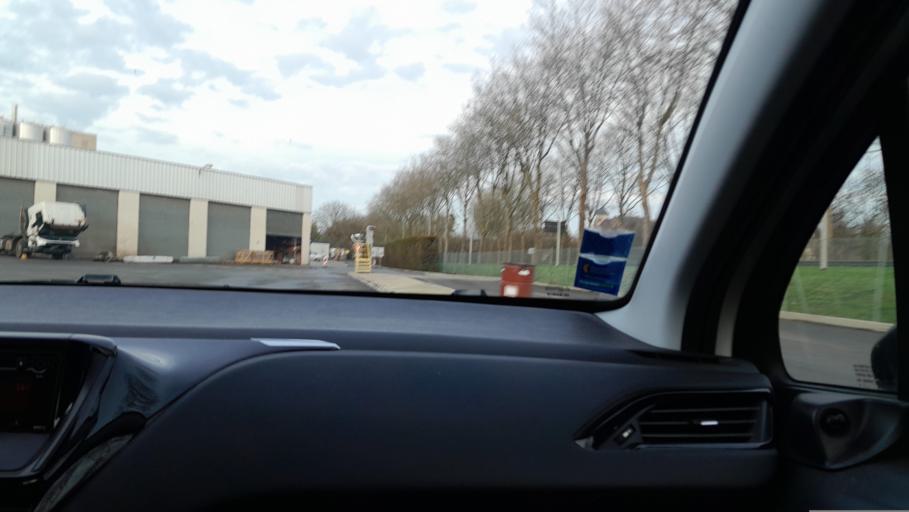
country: FR
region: Pays de la Loire
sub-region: Departement de la Mayenne
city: Craon
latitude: 47.8431
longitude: -0.9571
